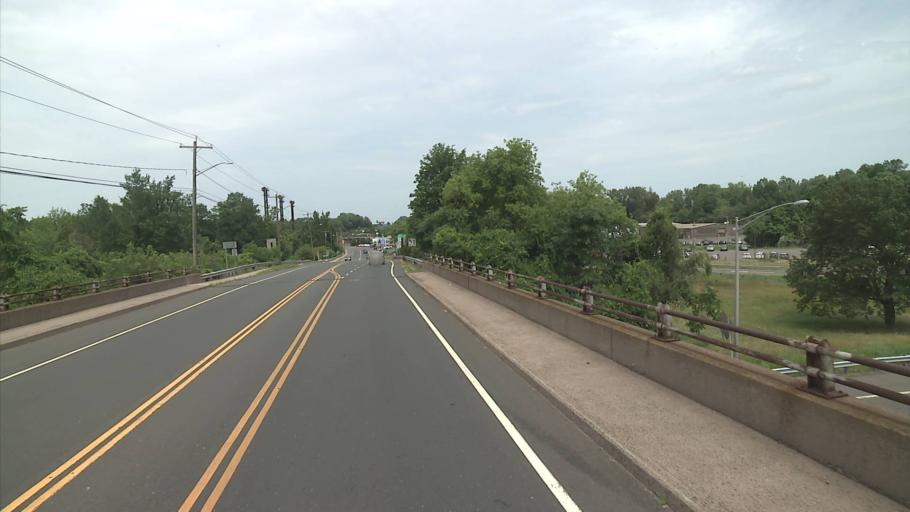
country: US
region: Connecticut
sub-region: Hartford County
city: Kensington
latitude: 41.6466
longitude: -72.7710
